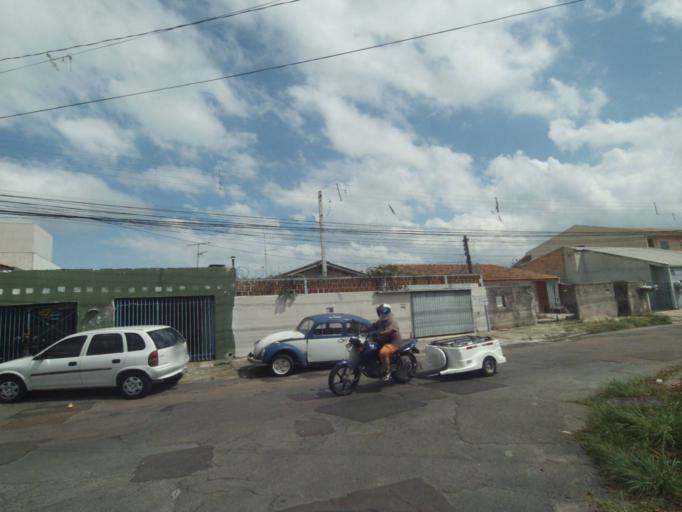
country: BR
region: Parana
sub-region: Pinhais
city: Pinhais
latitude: -25.4508
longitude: -49.2031
